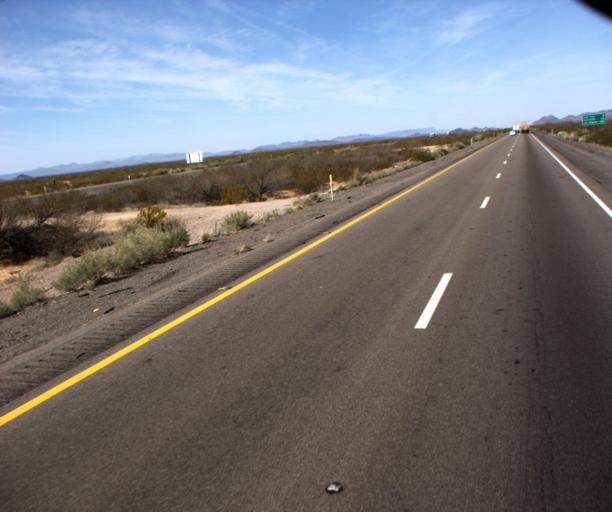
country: US
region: Arizona
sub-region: La Paz County
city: Salome
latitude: 33.5898
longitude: -113.4892
